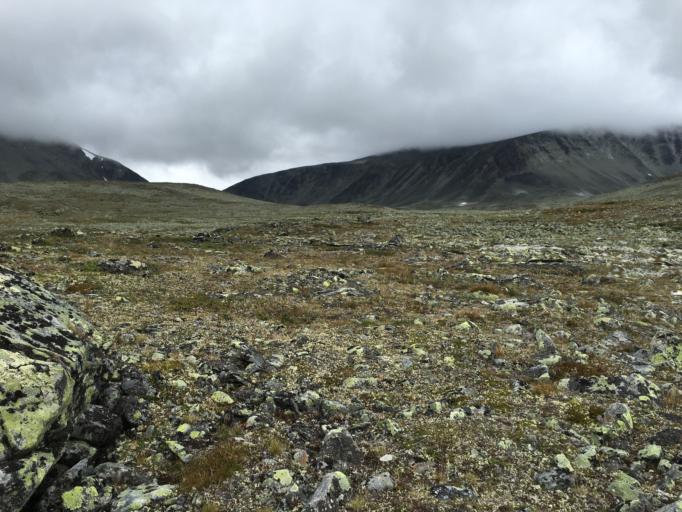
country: NO
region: Oppland
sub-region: Lom
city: Fossbergom
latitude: 61.5862
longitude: 8.7196
